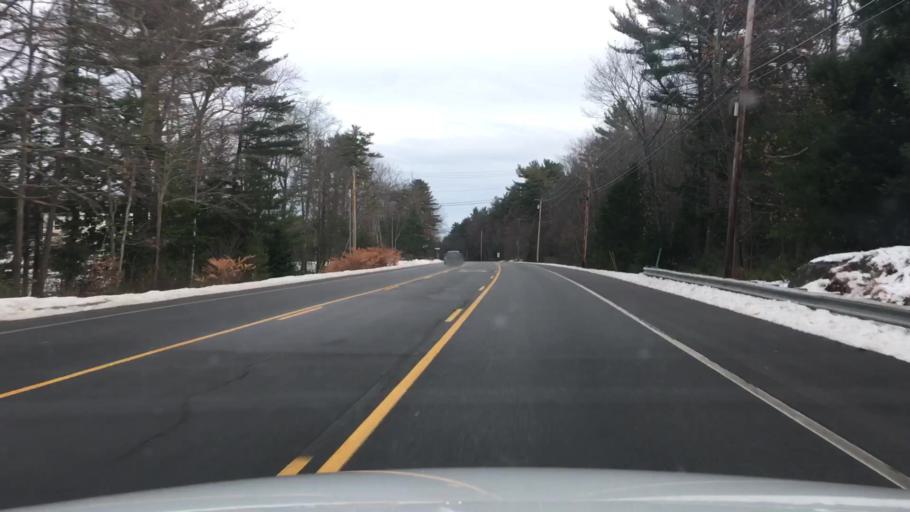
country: US
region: Maine
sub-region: Cumberland County
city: Falmouth Foreside
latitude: 43.7534
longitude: -70.2094
